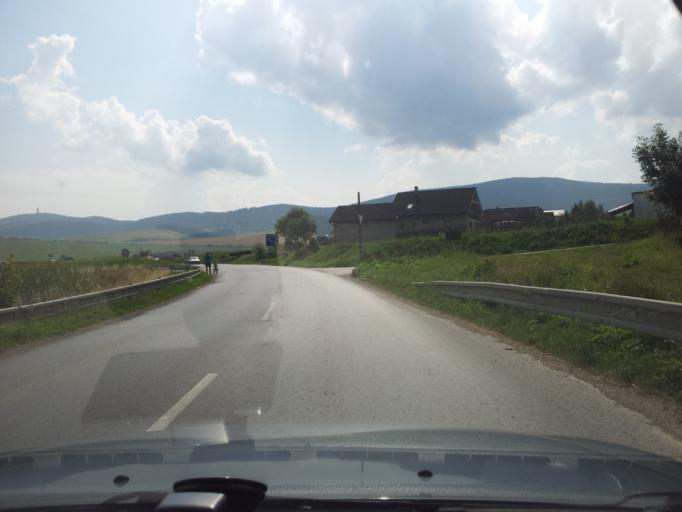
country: SK
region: Zilinsky
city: Namestovo
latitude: 49.3712
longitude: 19.4131
